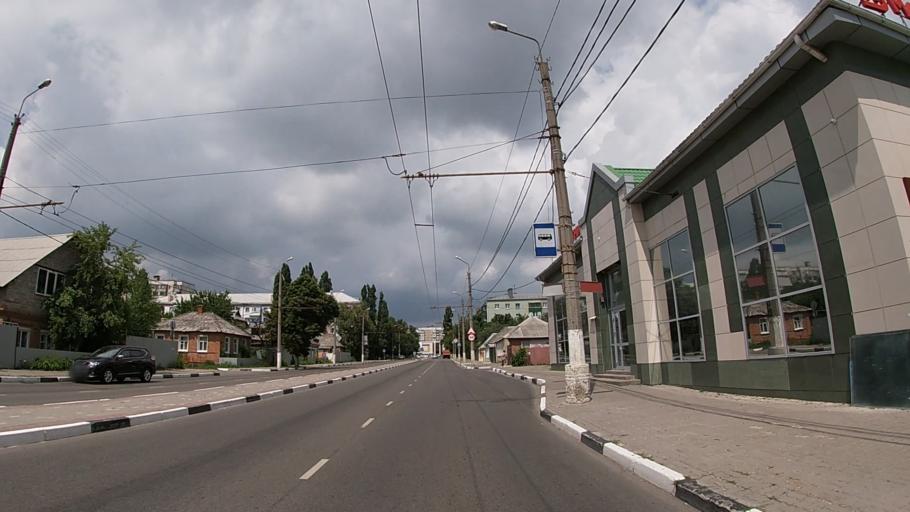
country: RU
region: Belgorod
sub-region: Belgorodskiy Rayon
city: Belgorod
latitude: 50.6101
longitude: 36.5919
